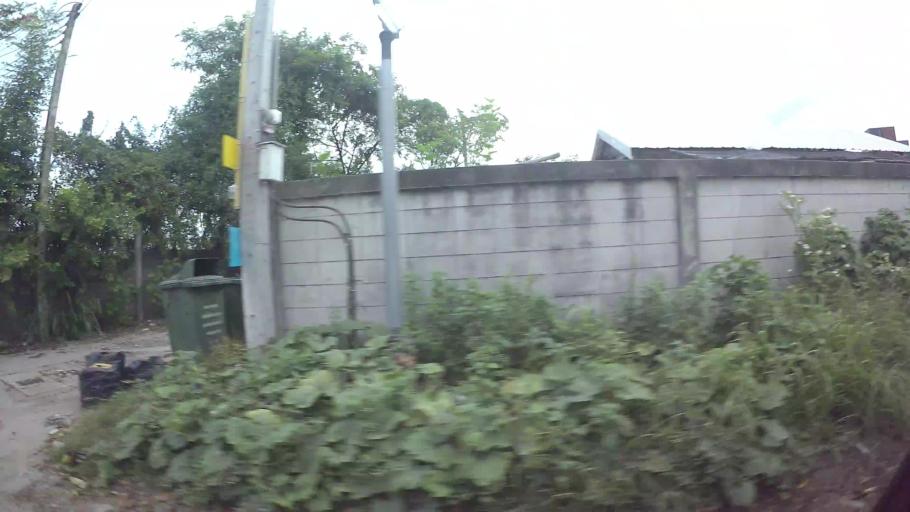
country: TH
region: Chon Buri
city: Ban Talat Bueng
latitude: 13.1228
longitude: 100.9722
